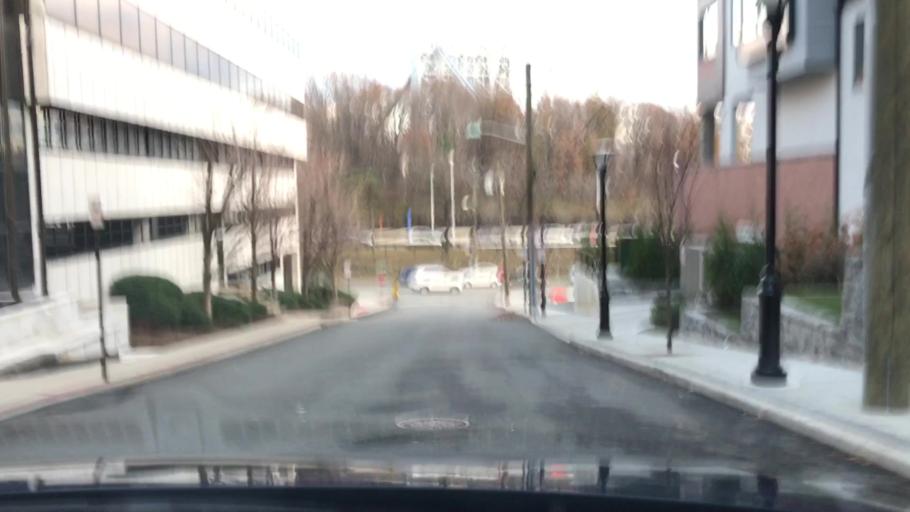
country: US
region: New Jersey
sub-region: Bergen County
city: Fort Lee
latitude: 40.8555
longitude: -73.9638
